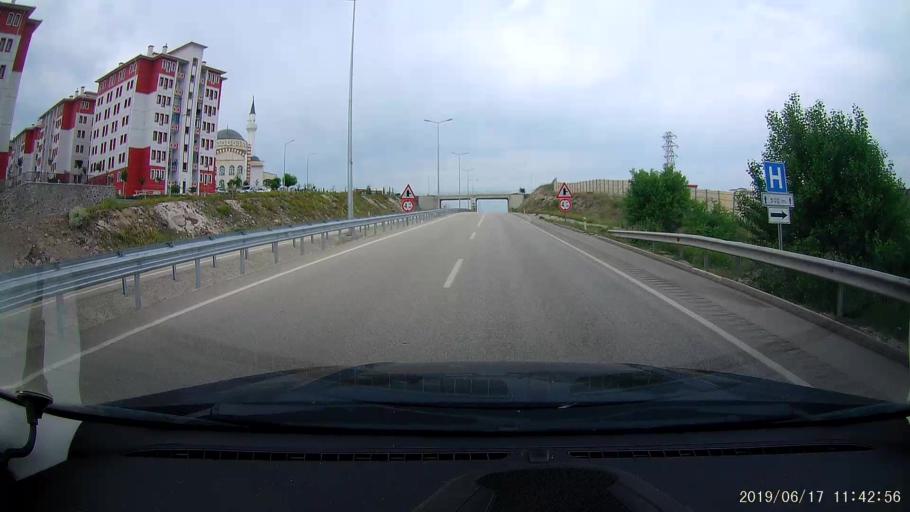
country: TR
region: Cankiri
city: Kursunlu
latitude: 40.8387
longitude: 33.2895
